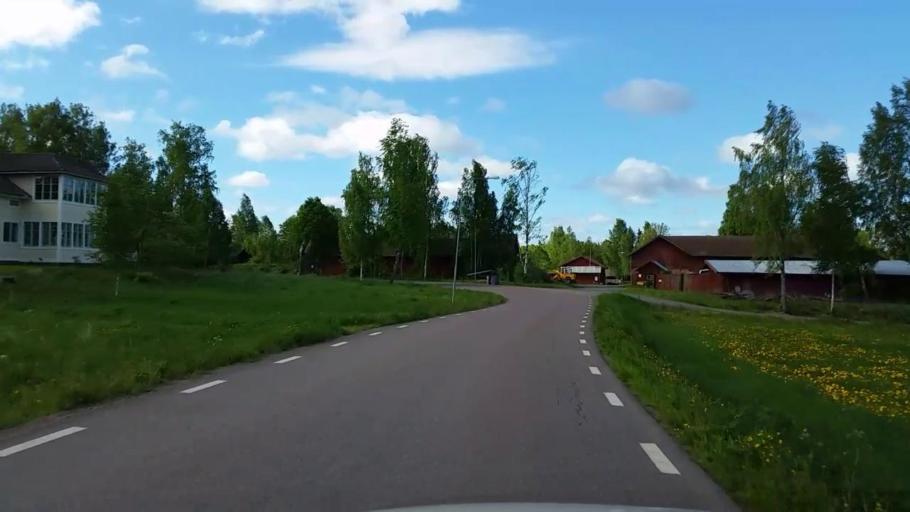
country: SE
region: Dalarna
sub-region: Borlange Kommun
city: Ornas
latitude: 60.5099
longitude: 15.5710
